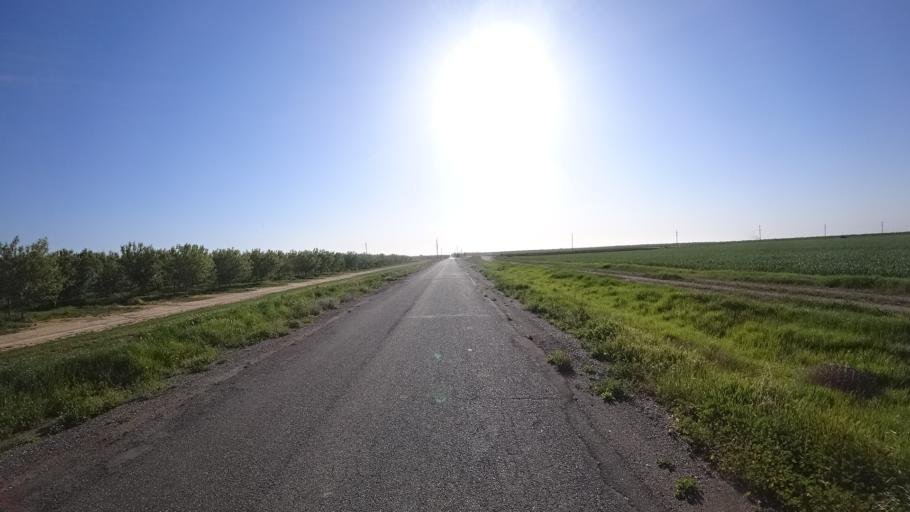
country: US
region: California
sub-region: Glenn County
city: Orland
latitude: 39.6822
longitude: -122.1811
